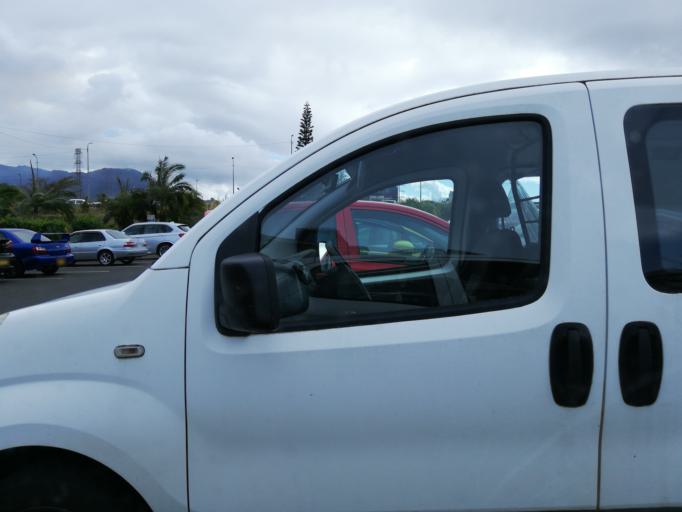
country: MU
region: Plaines Wilhems
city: Ebene
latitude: -20.2438
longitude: 57.4873
